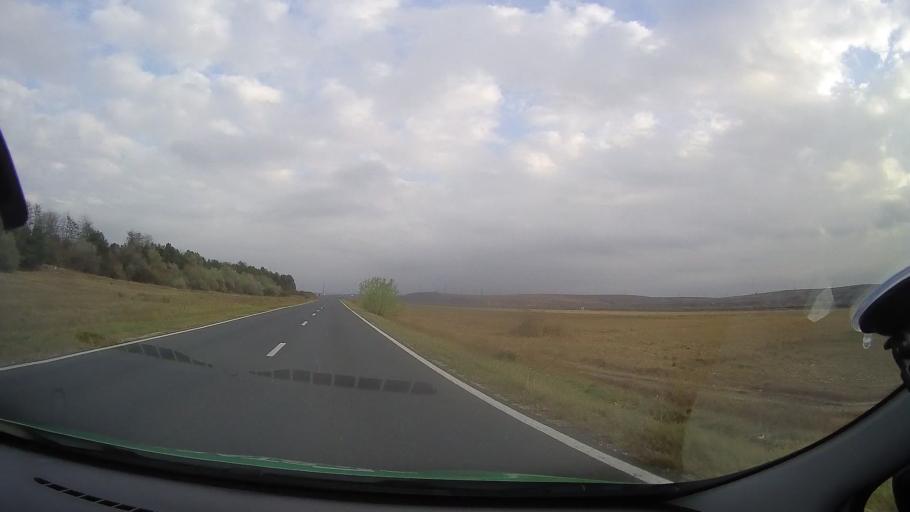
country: RO
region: Constanta
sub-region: Comuna Mircea Voda
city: Mircea Voda
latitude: 44.2691
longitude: 28.1778
